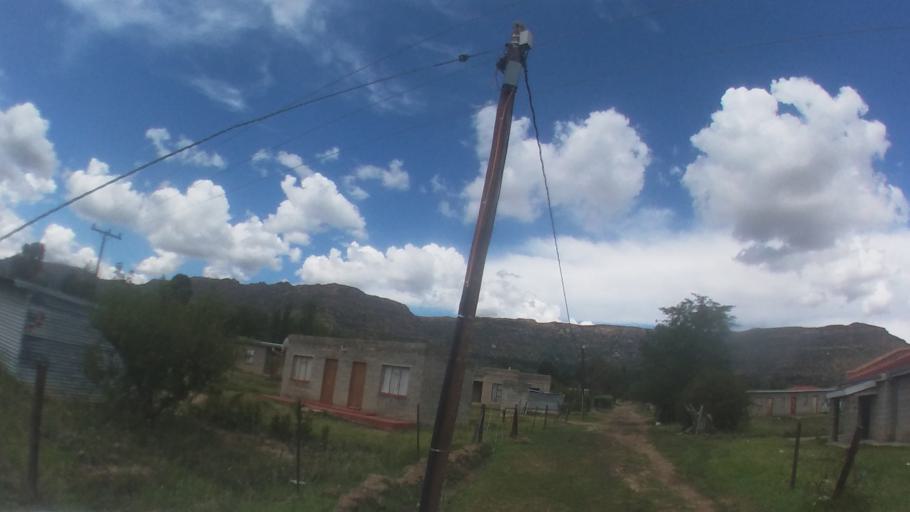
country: LS
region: Maseru
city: Nako
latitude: -29.6181
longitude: 27.5067
